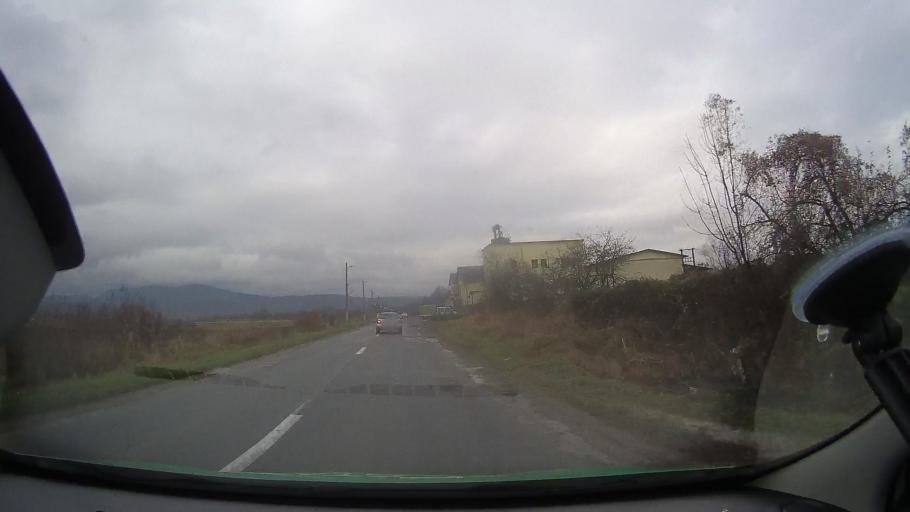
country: RO
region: Arad
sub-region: Comuna Buteni
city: Buteni
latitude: 46.3361
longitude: 22.1268
